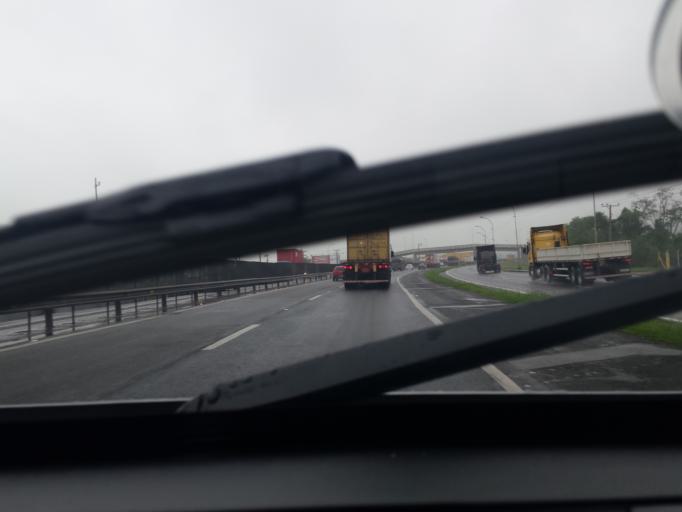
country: BR
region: Santa Catarina
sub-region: Itajai
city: Itajai
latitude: -26.8508
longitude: -48.7259
